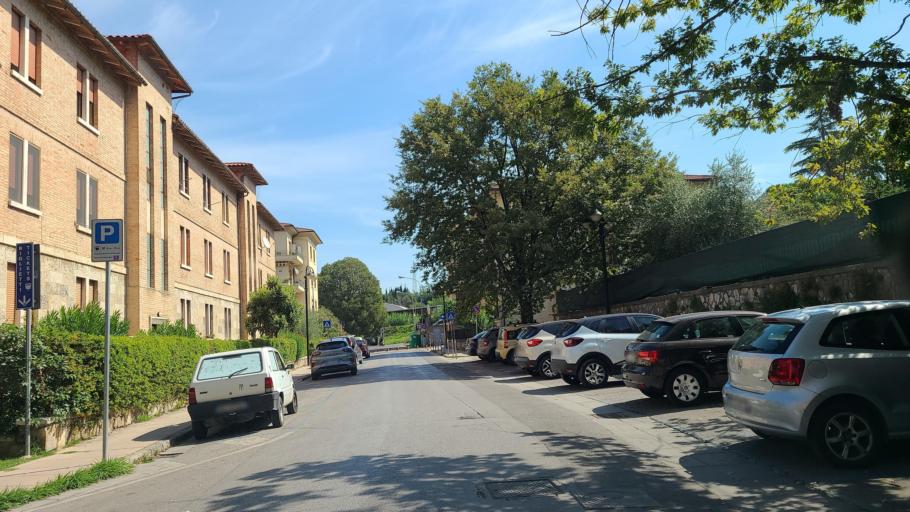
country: IT
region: Tuscany
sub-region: Provincia di Siena
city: Colle di Val d'Elsa
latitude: 43.4202
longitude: 11.1287
